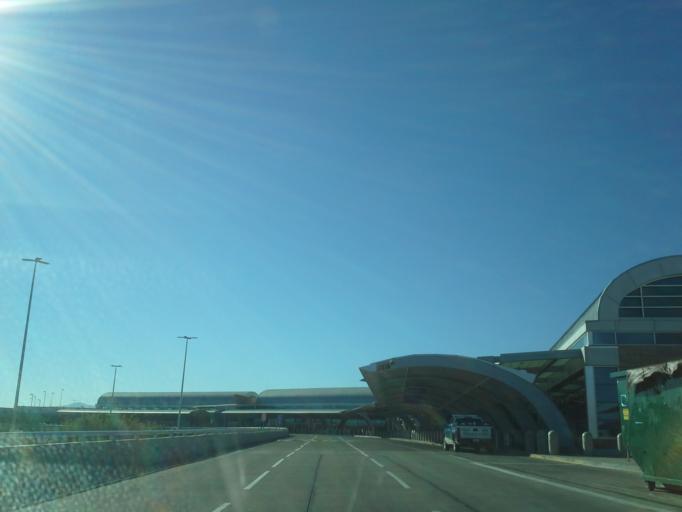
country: US
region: Arizona
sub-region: Pima County
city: Summit
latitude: 32.1218
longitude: -110.9378
